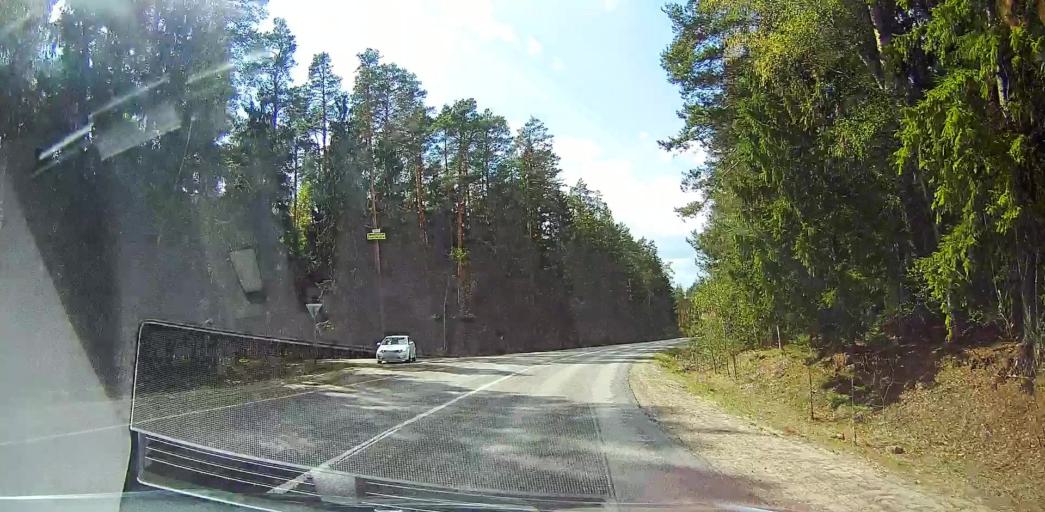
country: RU
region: Moskovskaya
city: Davydovo
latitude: 55.5616
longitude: 38.8509
